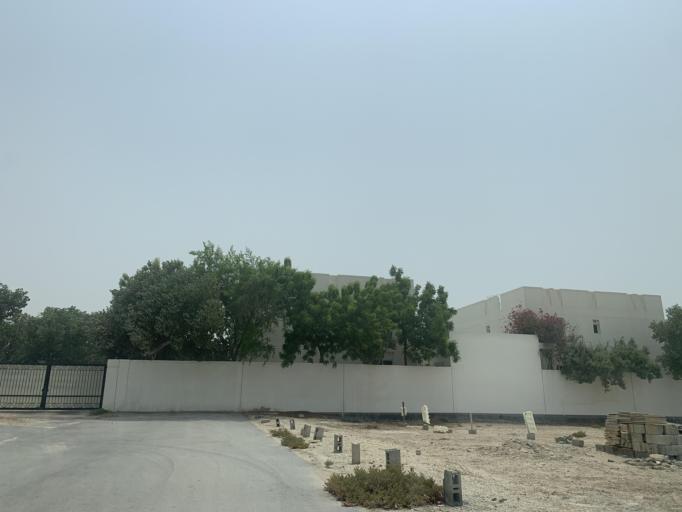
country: BH
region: Central Governorate
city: Madinat Hamad
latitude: 26.1670
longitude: 50.4703
